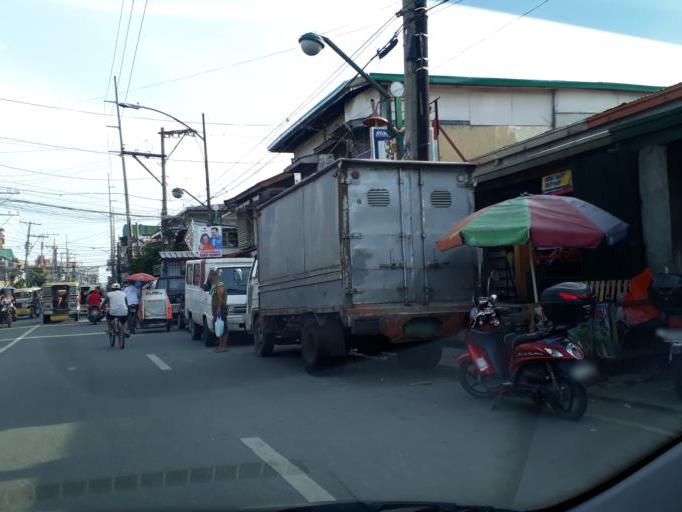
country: PH
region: Metro Manila
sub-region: City of Manila
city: Manila
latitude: 14.6315
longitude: 120.9745
